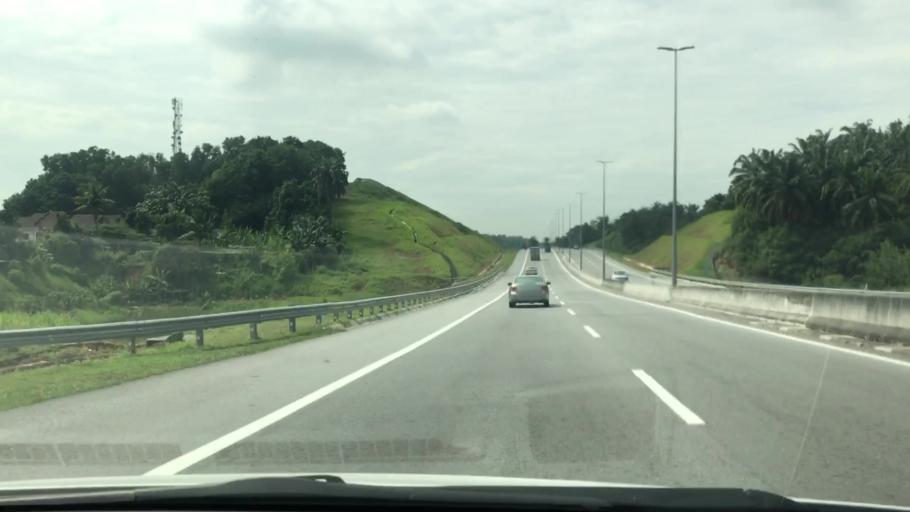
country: MY
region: Selangor
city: Kampong Baharu Balakong
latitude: 3.0099
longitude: 101.6875
